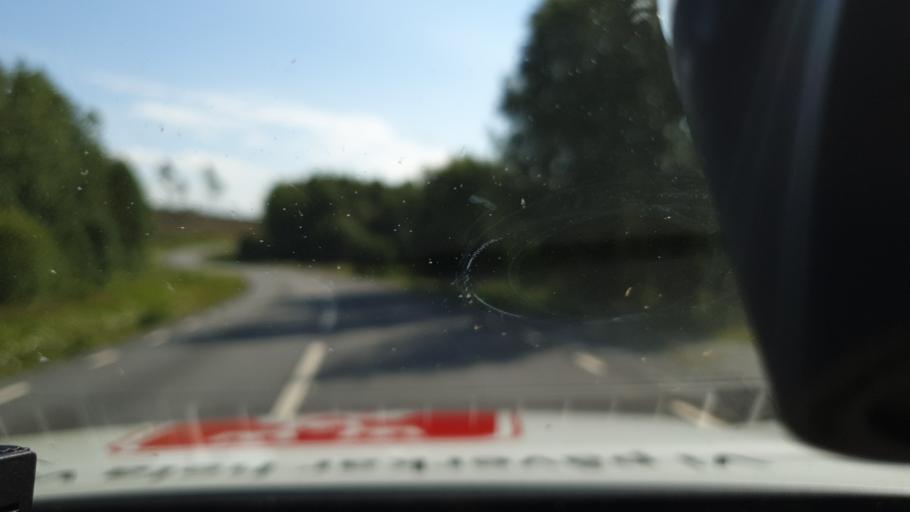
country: SE
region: Norrbotten
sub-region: Bodens Kommun
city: Saevast
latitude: 65.8355
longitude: 21.8497
